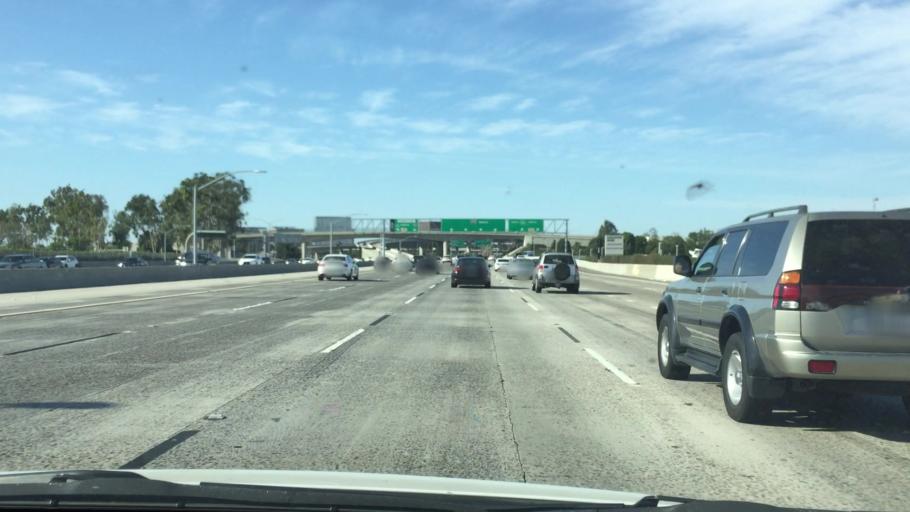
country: US
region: California
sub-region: Orange County
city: Irvine
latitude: 33.6851
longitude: -117.8620
